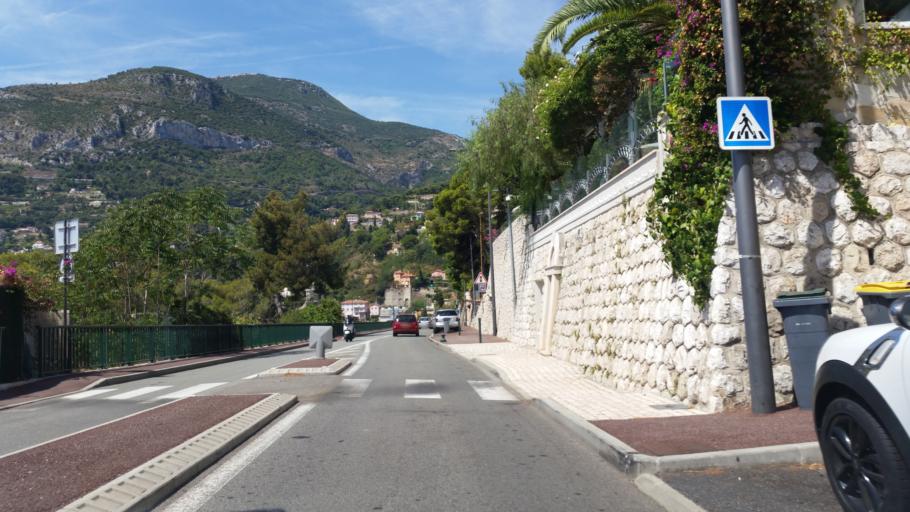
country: FR
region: Provence-Alpes-Cote d'Azur
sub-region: Departement des Alpes-Maritimes
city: Roquebrune-Cap-Martin
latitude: 43.7596
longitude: 7.4662
